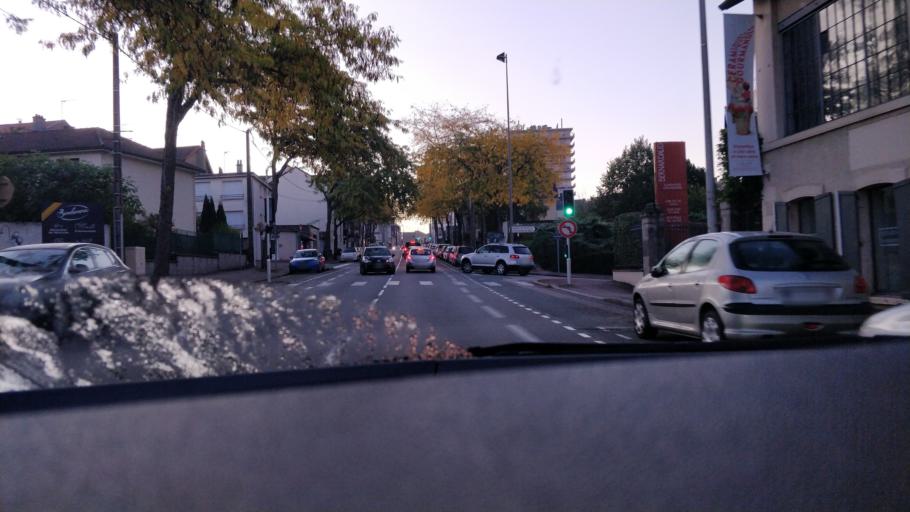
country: FR
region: Limousin
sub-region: Departement de la Haute-Vienne
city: Limoges
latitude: 45.8352
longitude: 1.2451
